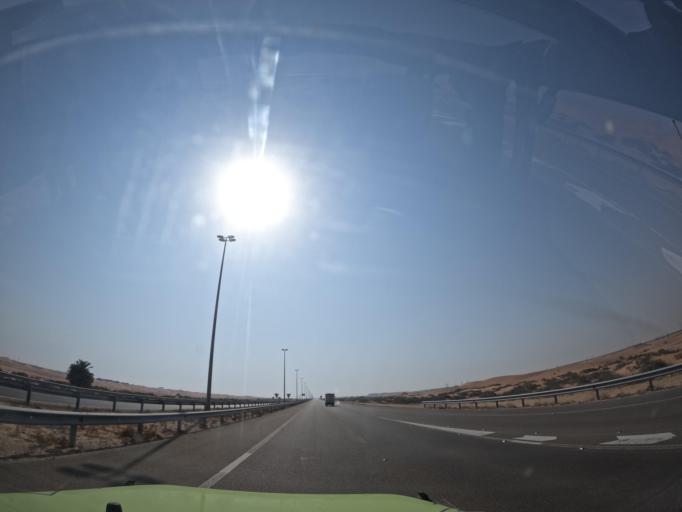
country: OM
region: Al Buraimi
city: Al Buraymi
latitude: 24.5092
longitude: 55.5694
